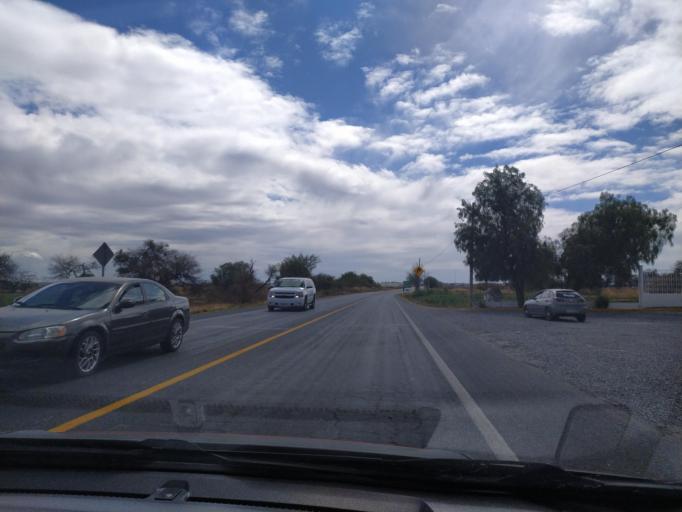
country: LA
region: Oudomxai
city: Muang La
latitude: 21.0142
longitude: 101.8279
